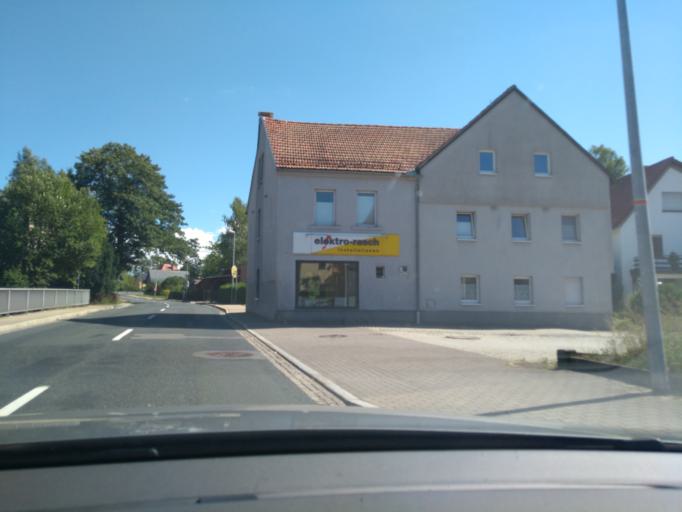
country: DE
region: Saxony
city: Grossrohrsdorf
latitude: 51.1431
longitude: 14.0335
